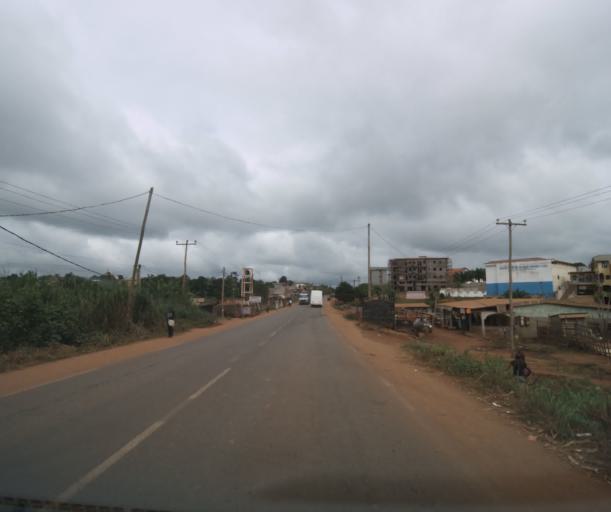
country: CM
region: Centre
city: Yaounde
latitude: 3.7947
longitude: 11.4914
